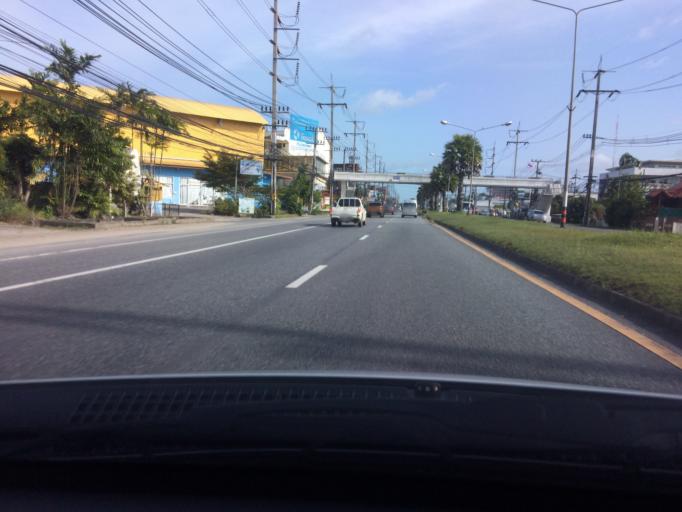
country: TH
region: Phuket
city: Thalang
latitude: 7.9910
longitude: 98.3546
